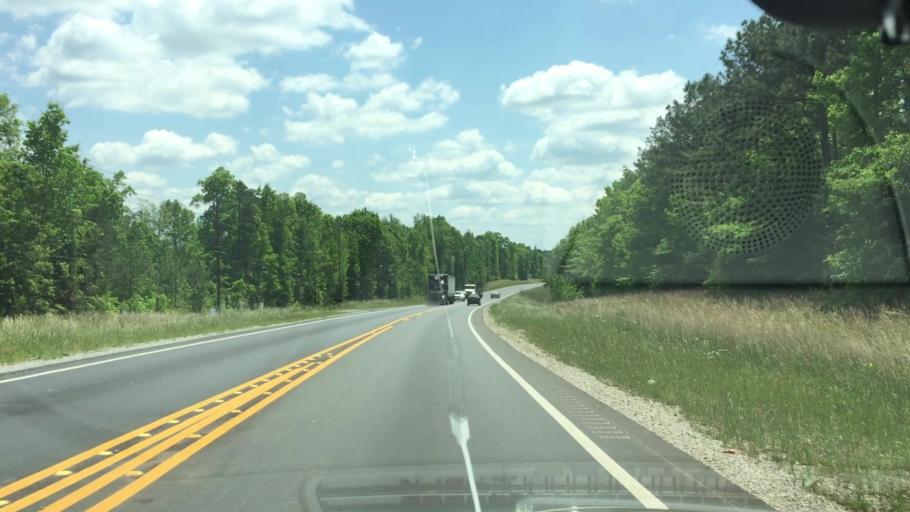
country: US
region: Alabama
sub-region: Lee County
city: Opelika
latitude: 32.6631
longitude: -85.3634
